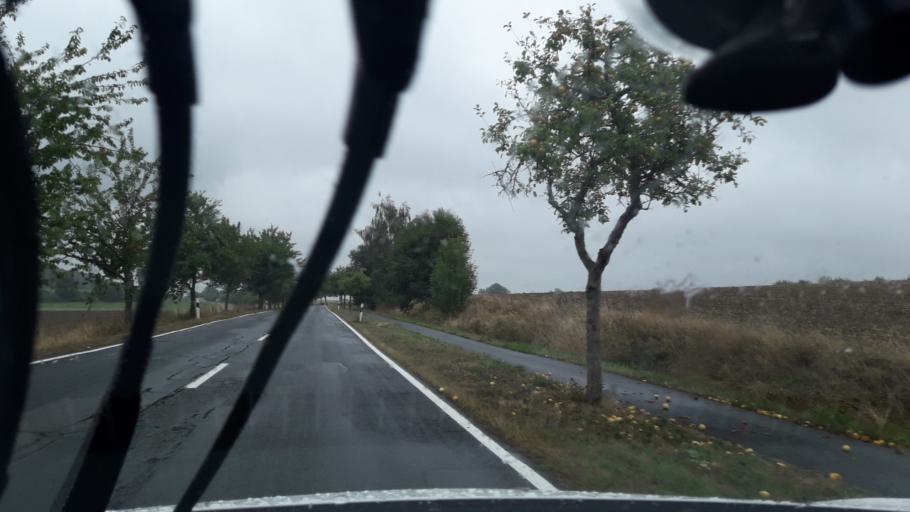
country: DE
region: Lower Saxony
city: Vienenburg
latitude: 51.9641
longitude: 10.5159
